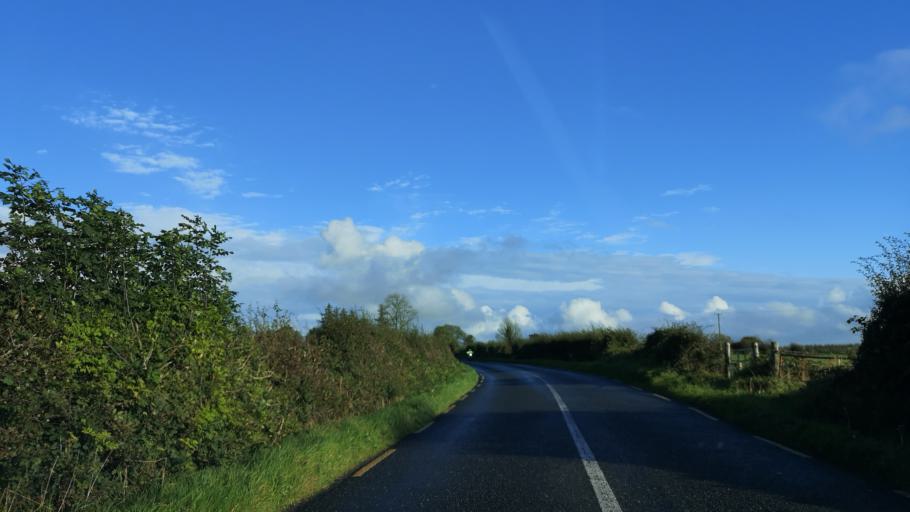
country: IE
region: Connaught
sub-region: Roscommon
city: Castlerea
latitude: 53.8103
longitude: -8.5225
